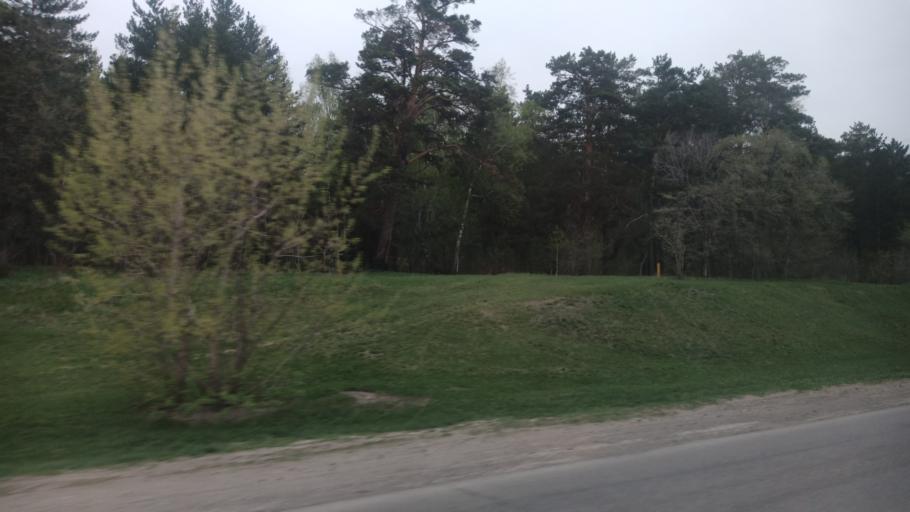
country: RU
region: Altai Krai
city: Yuzhnyy
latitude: 53.2618
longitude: 83.7022
